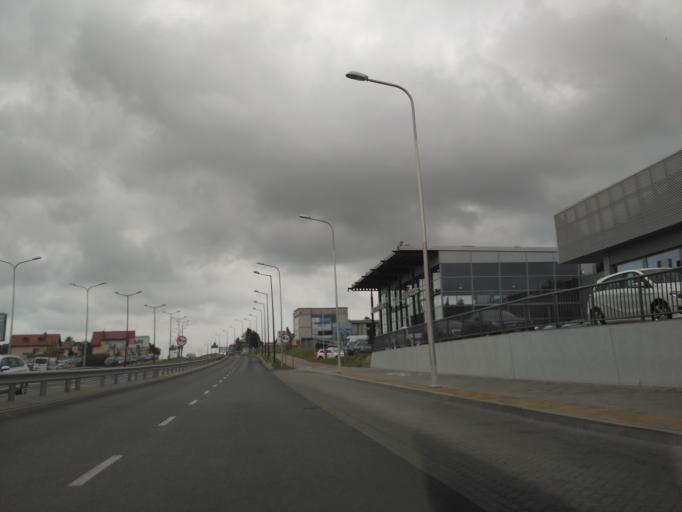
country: PL
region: Lublin Voivodeship
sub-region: Powiat lubelski
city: Lublin
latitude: 51.2801
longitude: 22.5746
